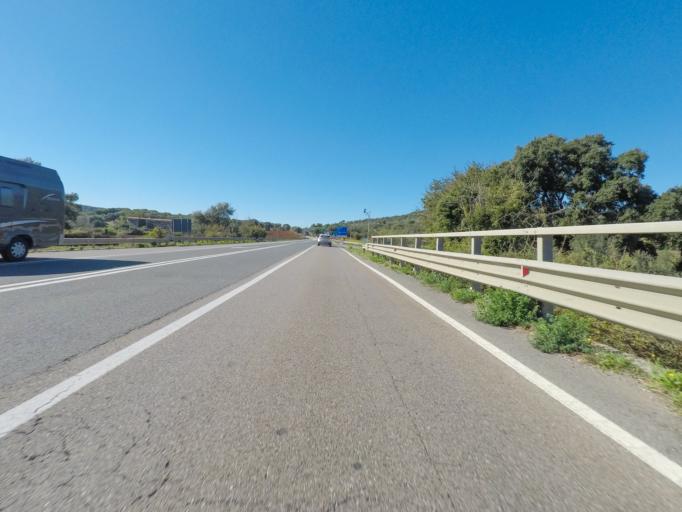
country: IT
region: Tuscany
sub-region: Provincia di Grosseto
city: Orbetello Scalo
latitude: 42.4179
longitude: 11.3057
